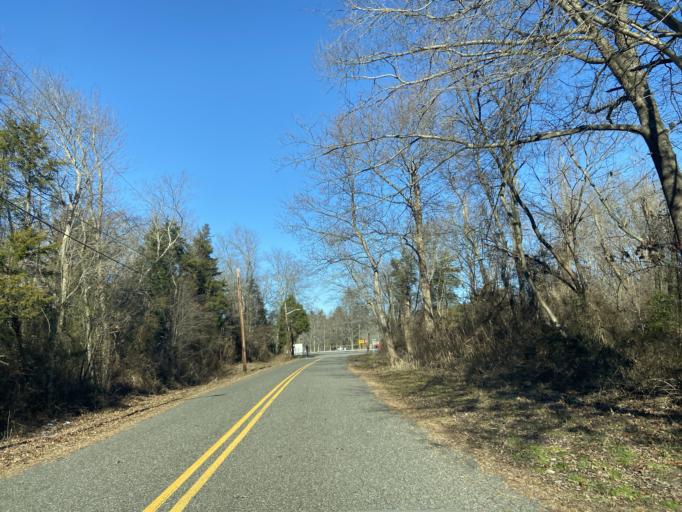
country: US
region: New Jersey
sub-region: Cumberland County
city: Vineland
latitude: 39.4947
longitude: -75.0750
